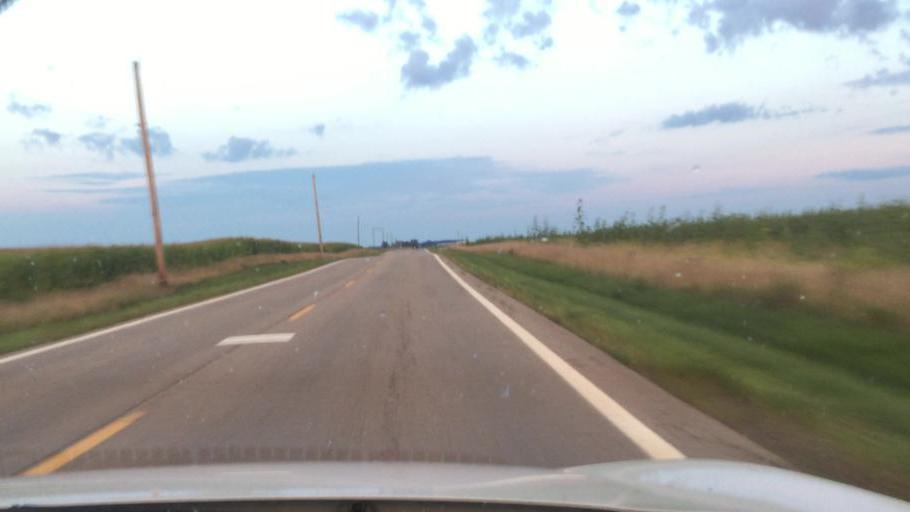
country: US
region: Ohio
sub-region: Madison County
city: Choctaw Lake
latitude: 40.0140
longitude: -83.4591
